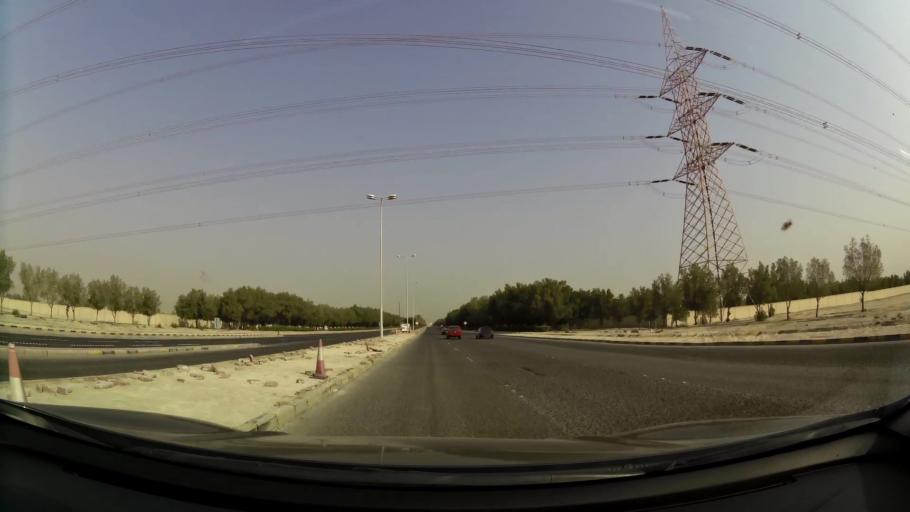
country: KW
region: Al Asimah
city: Ar Rabiyah
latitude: 29.2960
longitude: 47.8321
